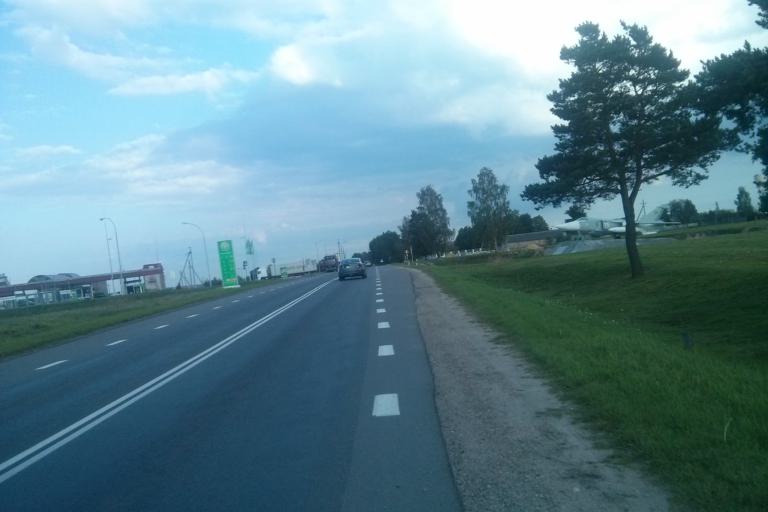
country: BY
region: Minsk
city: Chervyen'
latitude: 53.7222
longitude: 28.3857
